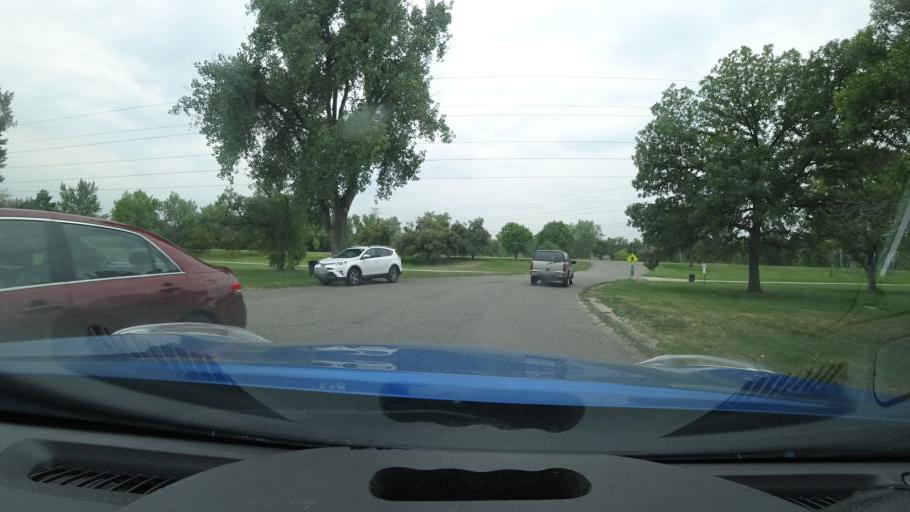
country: US
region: Colorado
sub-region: Arapahoe County
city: Glendale
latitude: 39.6945
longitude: -104.9167
